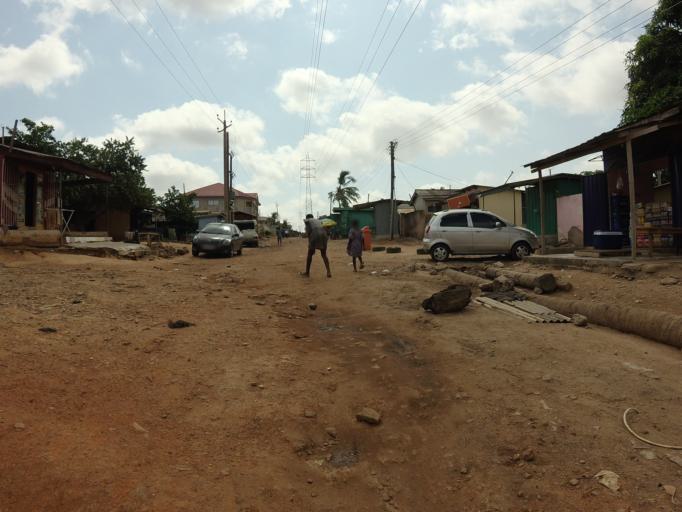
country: GH
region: Greater Accra
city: Dome
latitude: 5.6173
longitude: -0.2470
